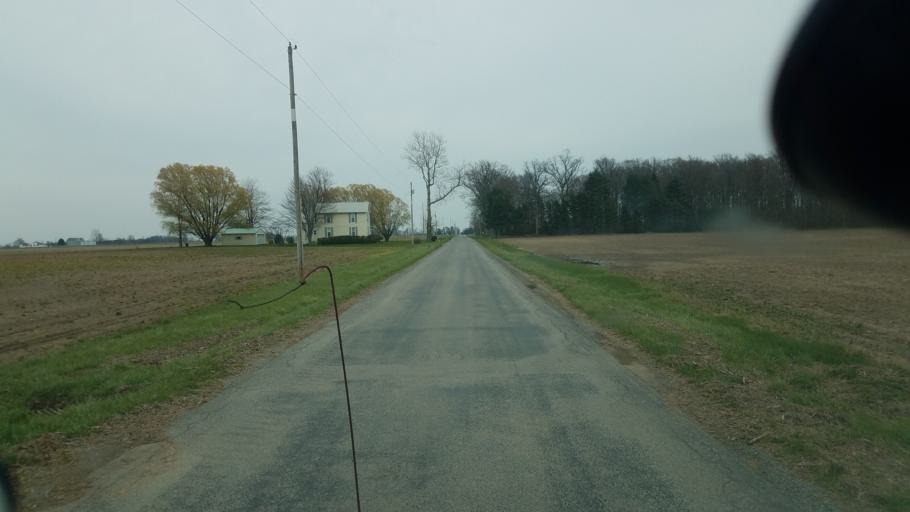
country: US
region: Ohio
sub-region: Hardin County
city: Forest
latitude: 40.8908
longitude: -83.5239
